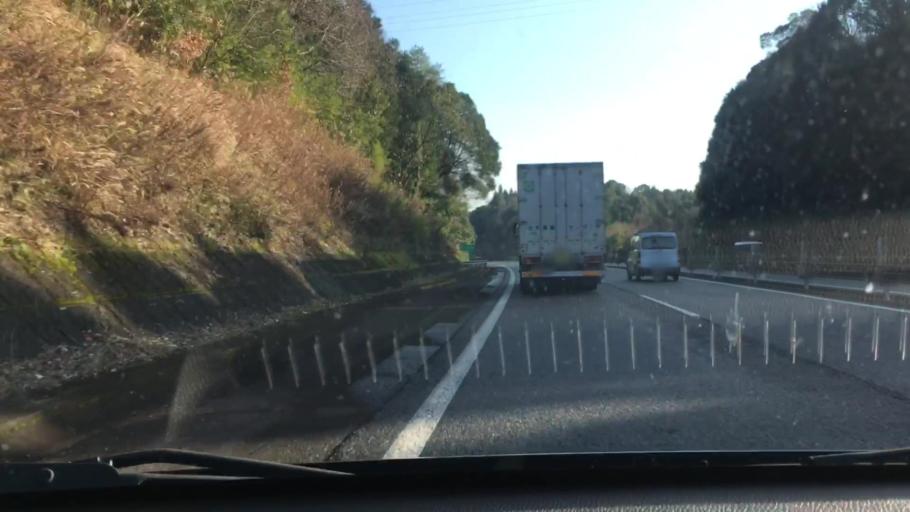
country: JP
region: Kagoshima
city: Okuchi-shinohara
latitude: 31.9150
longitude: 130.7034
